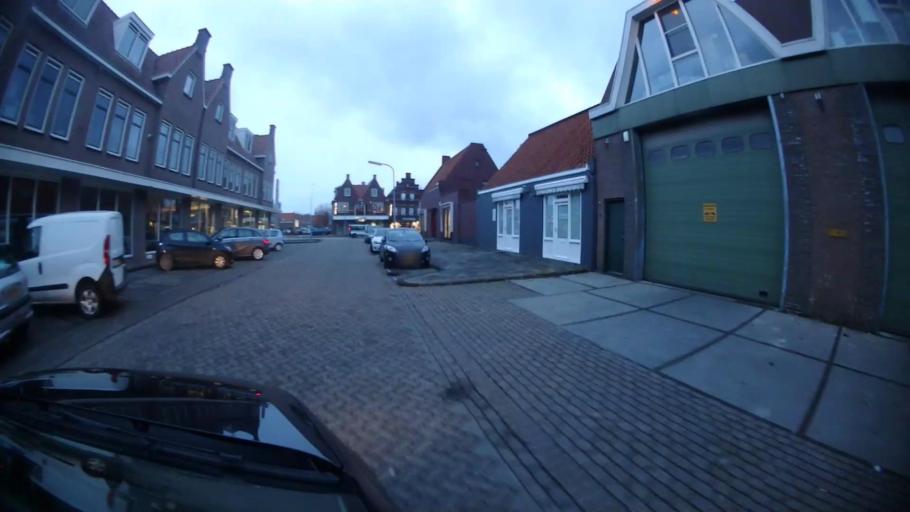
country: NL
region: North Holland
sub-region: Gemeente Edam-Volendam
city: Volendam
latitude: 52.4945
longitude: 5.0708
